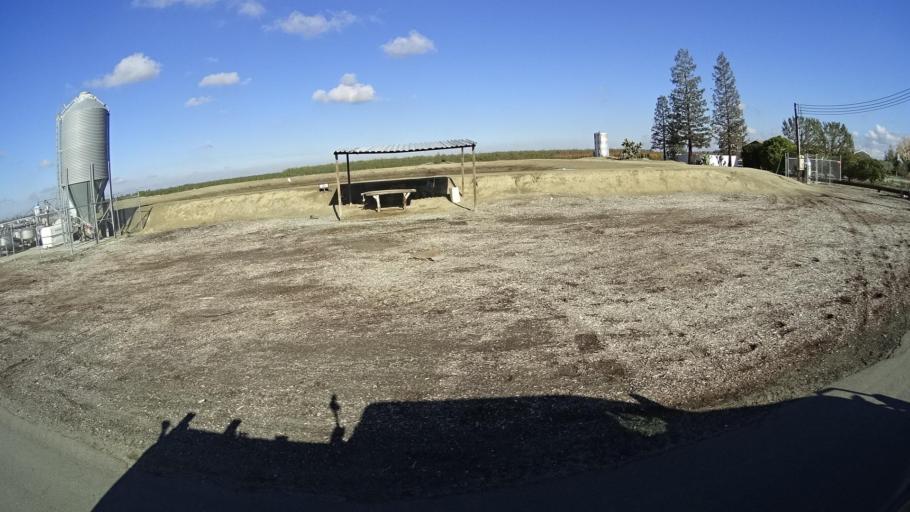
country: US
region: California
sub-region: Kern County
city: McFarland
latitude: 35.6597
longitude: -119.2481
